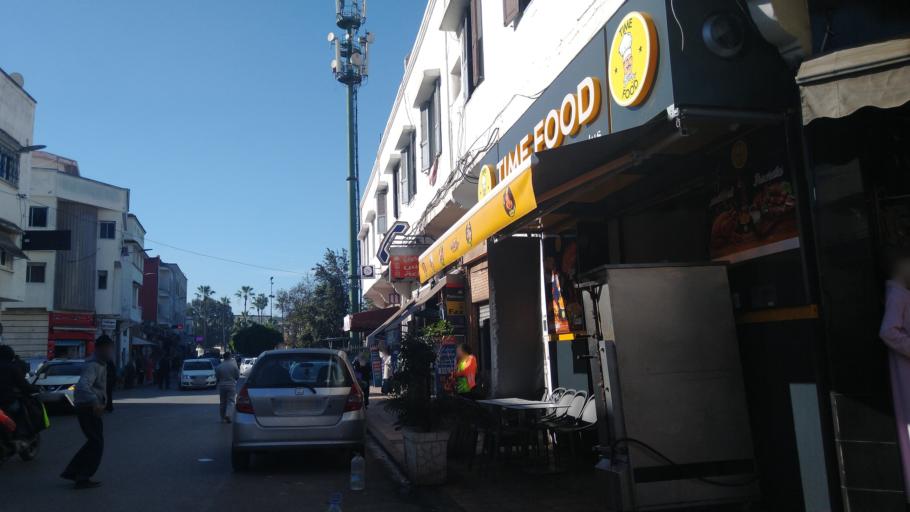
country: MA
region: Rabat-Sale-Zemmour-Zaer
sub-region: Rabat
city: Rabat
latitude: 34.0360
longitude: -6.8224
